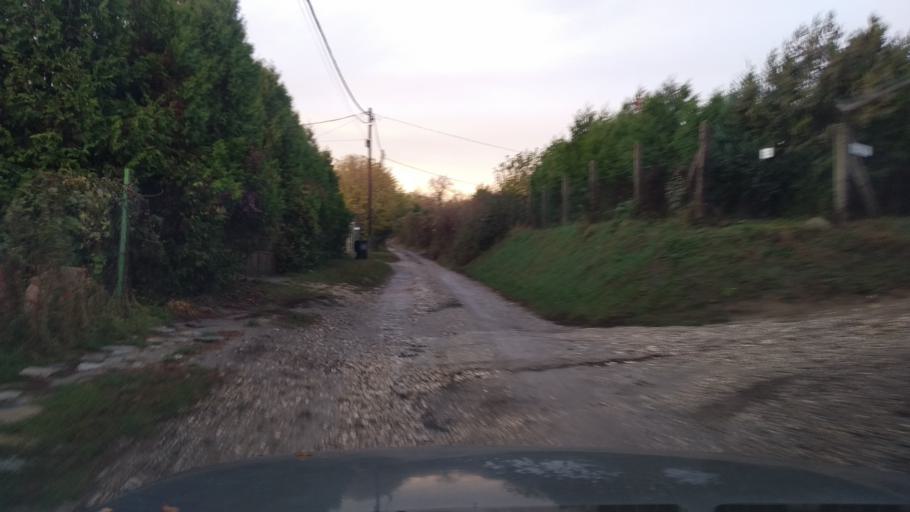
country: HU
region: Pest
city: Nagykovacsi
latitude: 47.6592
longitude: 18.9984
